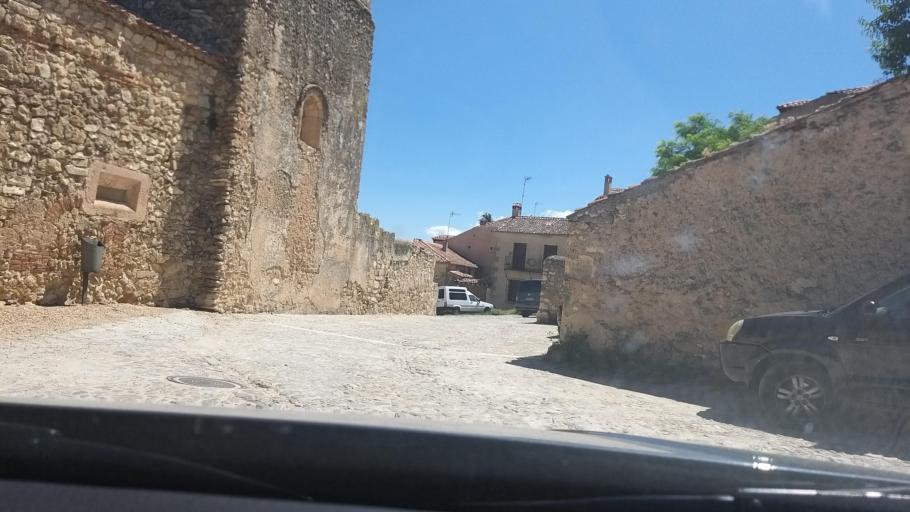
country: ES
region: Castille and Leon
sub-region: Provincia de Segovia
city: Pedraza
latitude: 41.1317
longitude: -3.8129
